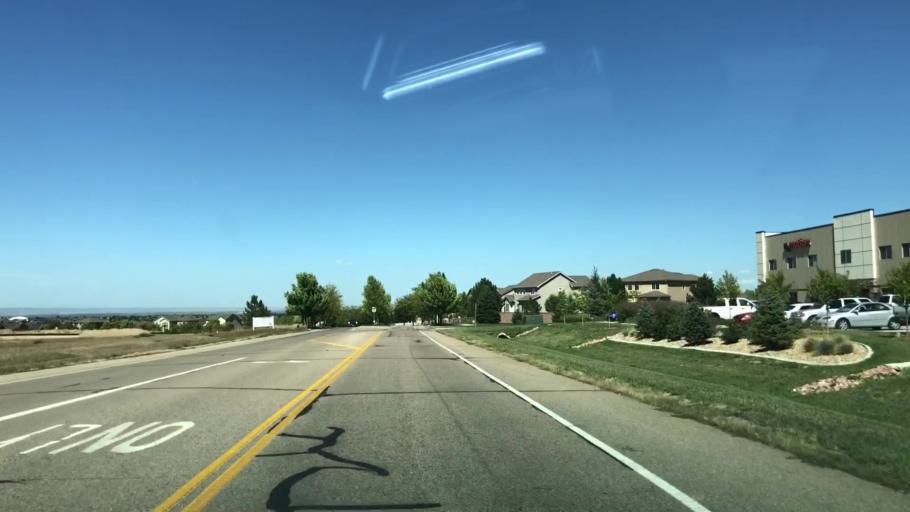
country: US
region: Colorado
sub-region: Weld County
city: Windsor
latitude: 40.4391
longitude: -104.9676
